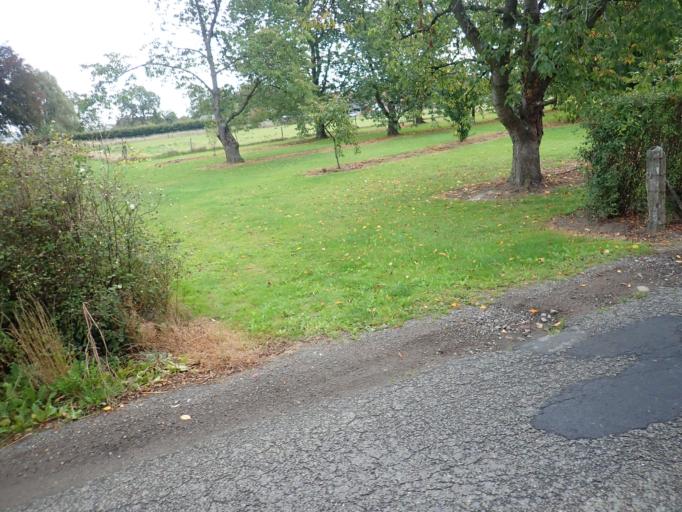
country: BE
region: Flanders
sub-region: Provincie Antwerpen
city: Ranst
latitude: 51.1823
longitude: 4.6066
